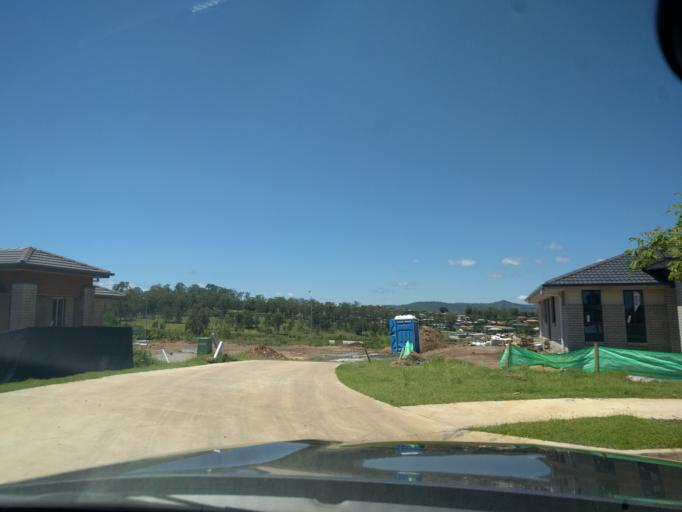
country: AU
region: Queensland
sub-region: Logan
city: Cedar Vale
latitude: -27.9878
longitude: 153.0126
